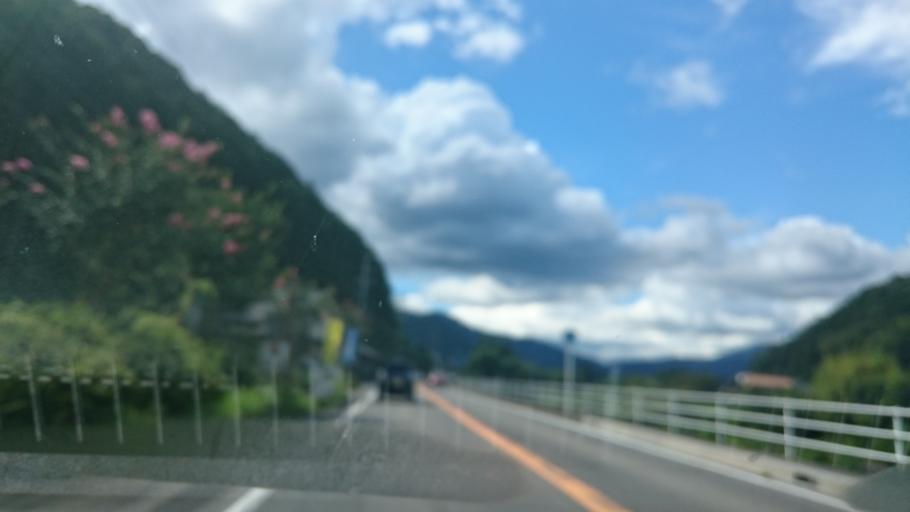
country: JP
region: Gifu
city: Nakatsugawa
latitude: 35.6325
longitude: 137.4498
